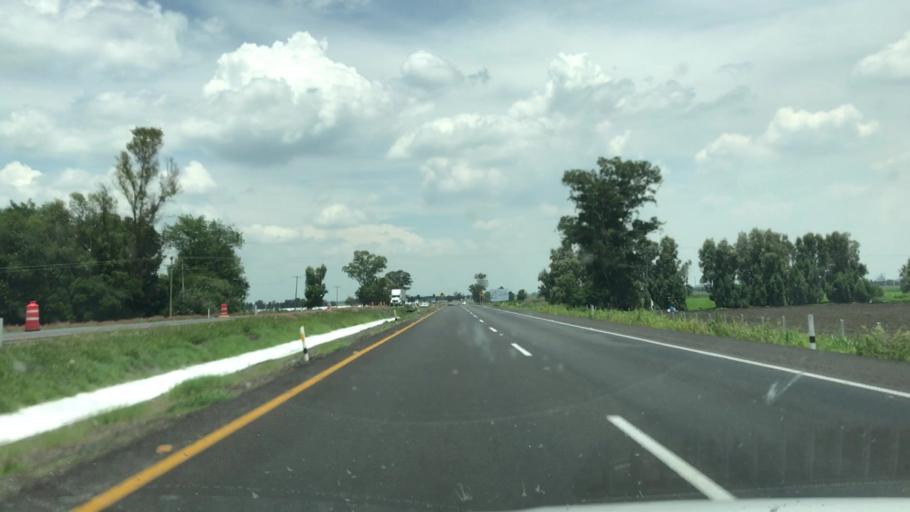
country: MX
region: Guanajuato
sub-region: Irapuato
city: Cuarta Brigada
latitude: 20.6422
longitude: -101.2686
